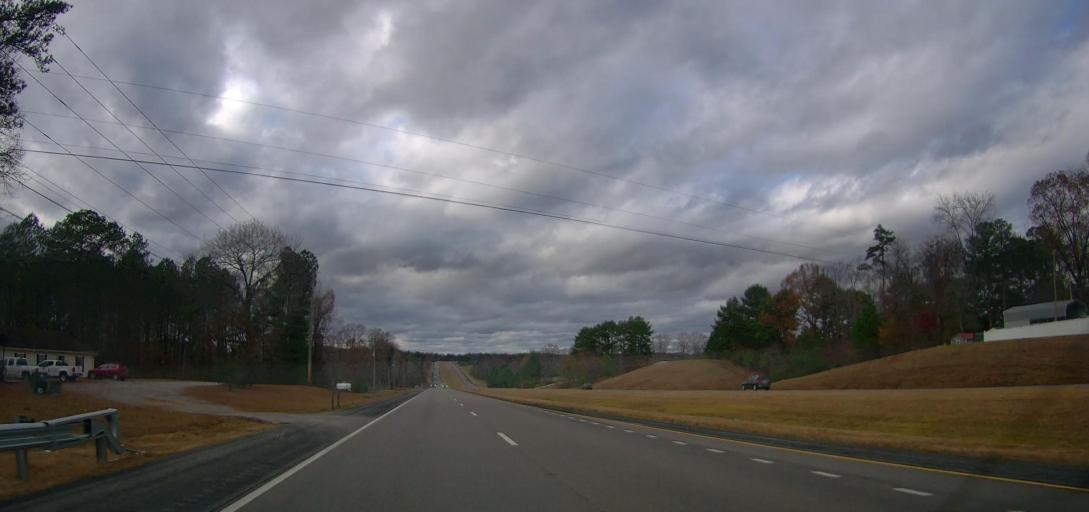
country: US
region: Alabama
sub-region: Morgan County
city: Falkville
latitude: 34.2536
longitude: -86.9735
